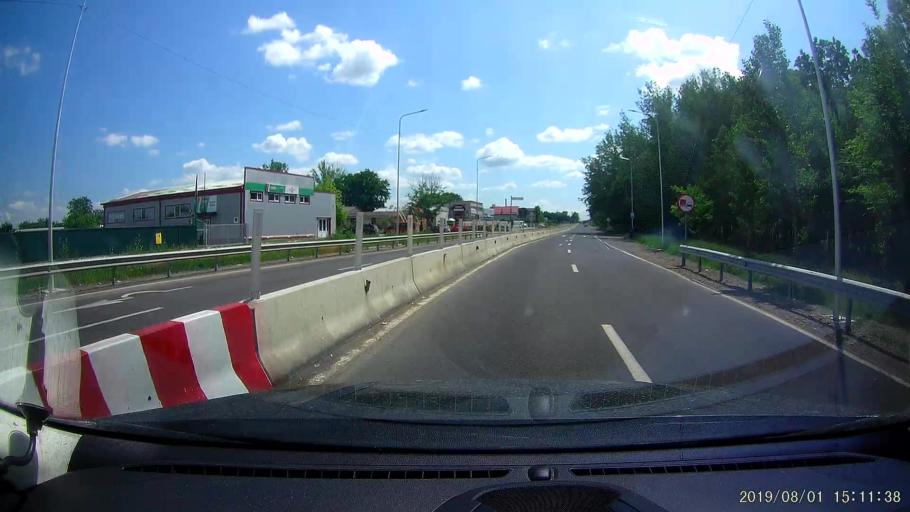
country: RO
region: Braila
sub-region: Comuna Chiscani
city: Chiscani
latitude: 45.2161
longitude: 27.9226
